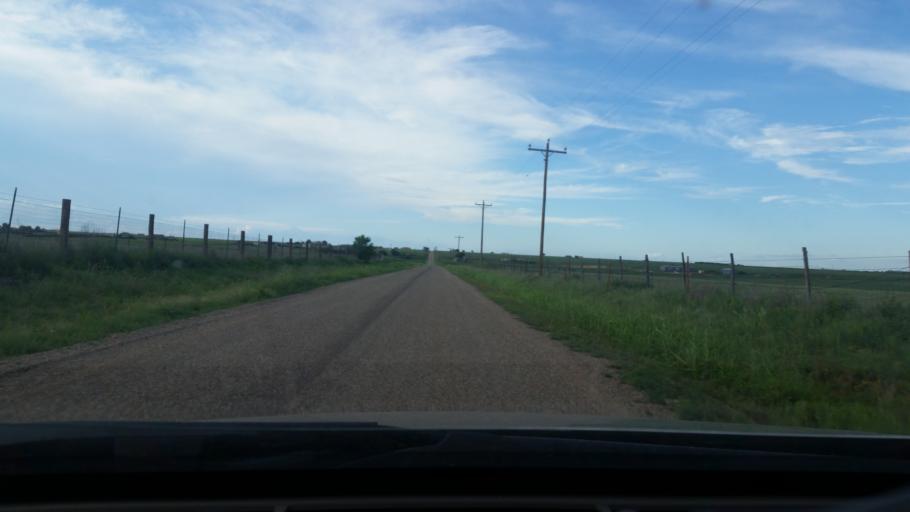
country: US
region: New Mexico
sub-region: Curry County
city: Clovis
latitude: 34.4711
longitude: -103.1789
